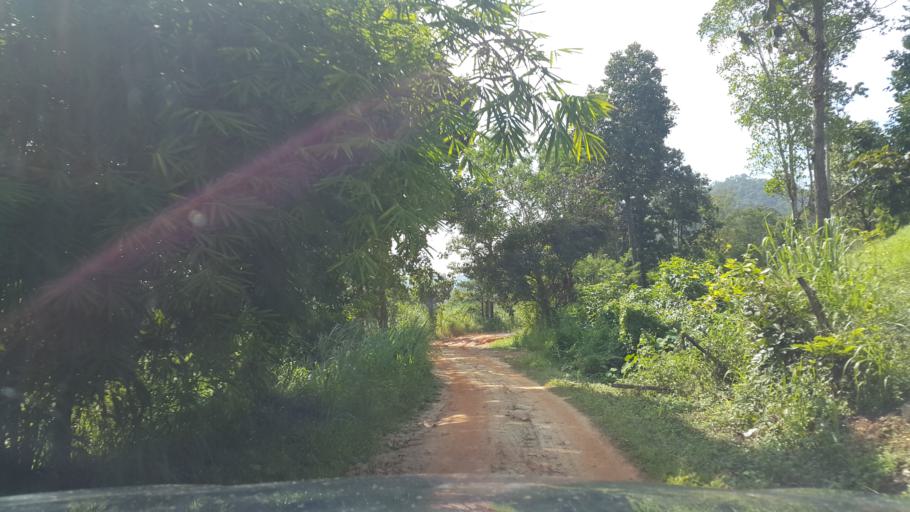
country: TH
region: Chiang Mai
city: Phrao
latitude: 19.0742
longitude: 99.2417
